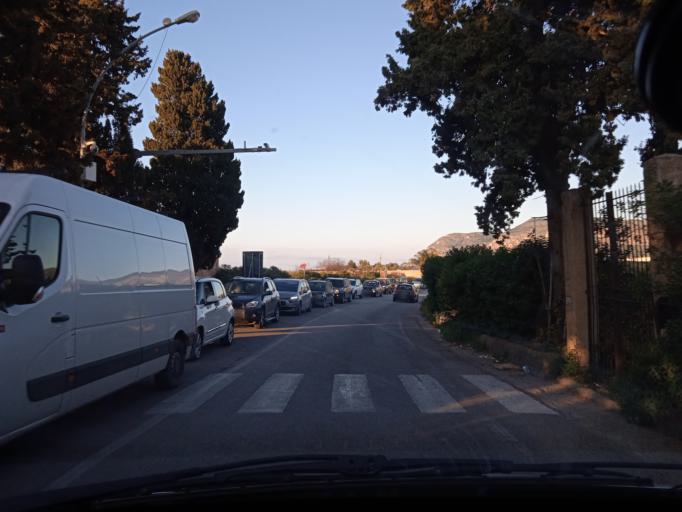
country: IT
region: Sicily
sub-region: Palermo
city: Ficarazzi
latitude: 38.0912
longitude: 13.4756
